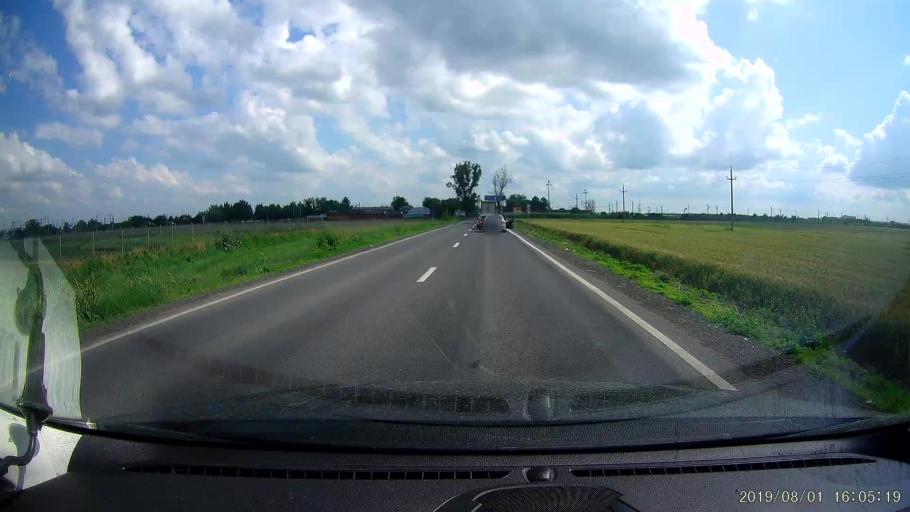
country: RO
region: Calarasi
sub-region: Comuna Dragalina
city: Drajna Noua
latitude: 44.4294
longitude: 27.3769
